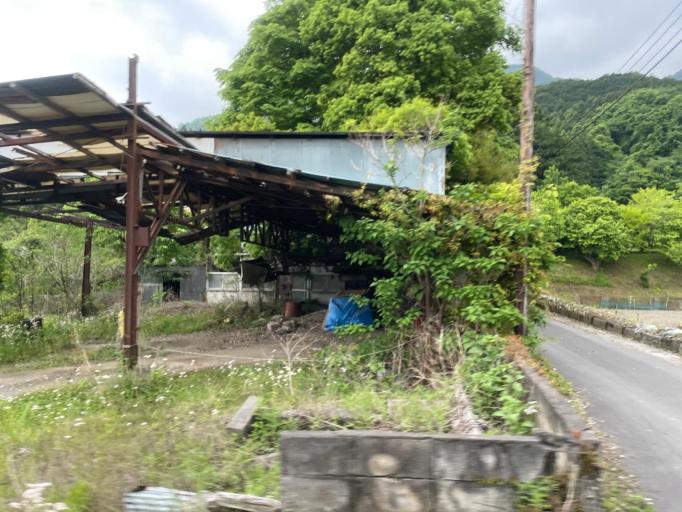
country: JP
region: Tochigi
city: Tanuma
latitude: 36.4600
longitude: 139.6361
